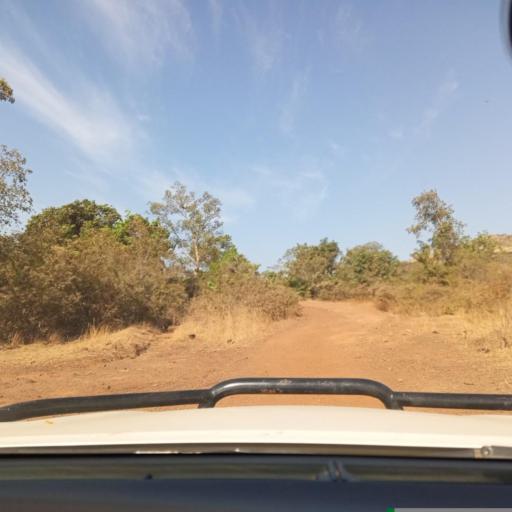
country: ML
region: Bamako
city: Bamako
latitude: 12.5554
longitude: -8.1413
